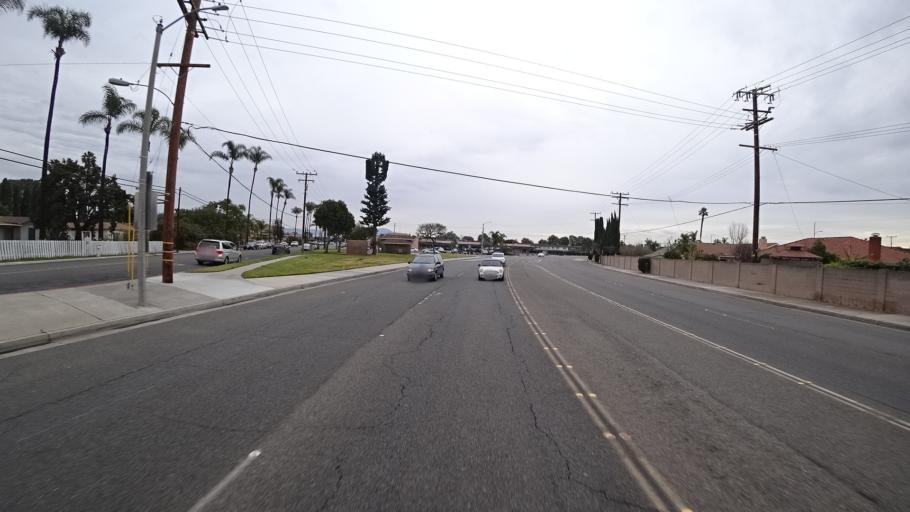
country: US
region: California
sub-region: Orange County
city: Fountain Valley
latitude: 33.7308
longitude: -117.9265
